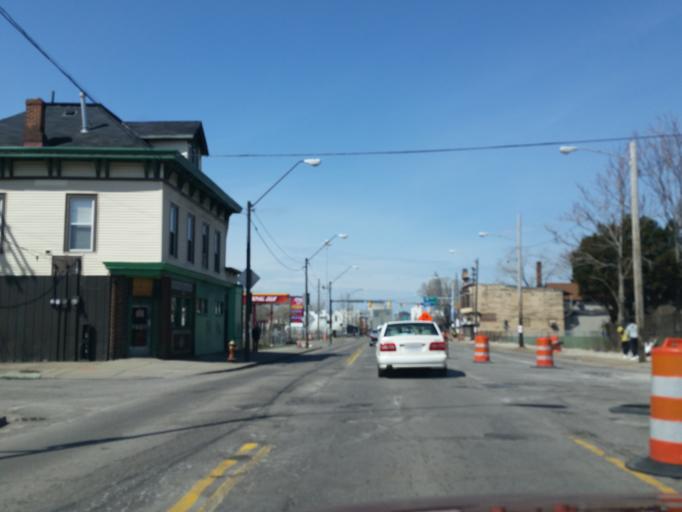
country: US
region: Ohio
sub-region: Cuyahoga County
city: Cleveland
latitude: 41.4725
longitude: -81.6995
